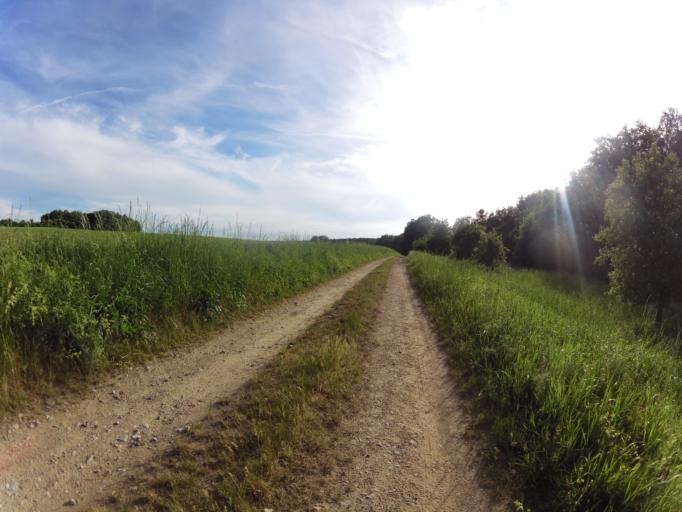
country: DE
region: Bavaria
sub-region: Regierungsbezirk Unterfranken
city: Ochsenfurt
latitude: 49.6986
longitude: 10.0652
